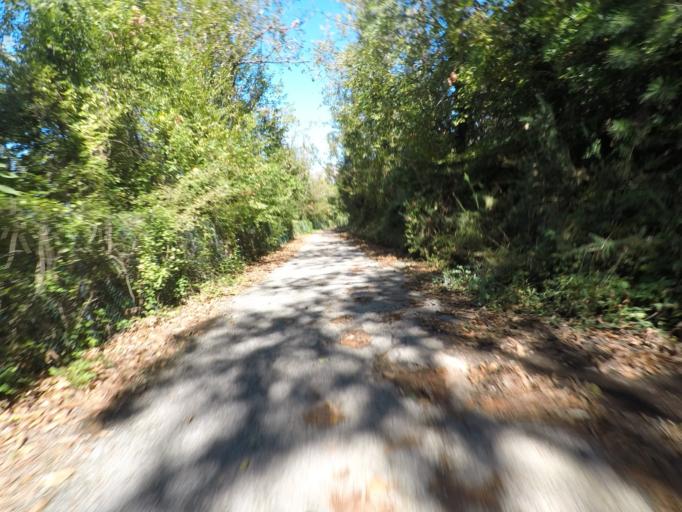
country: IT
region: Tuscany
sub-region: Provincia di Massa-Carrara
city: Montignoso
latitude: 44.0314
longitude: 10.1633
